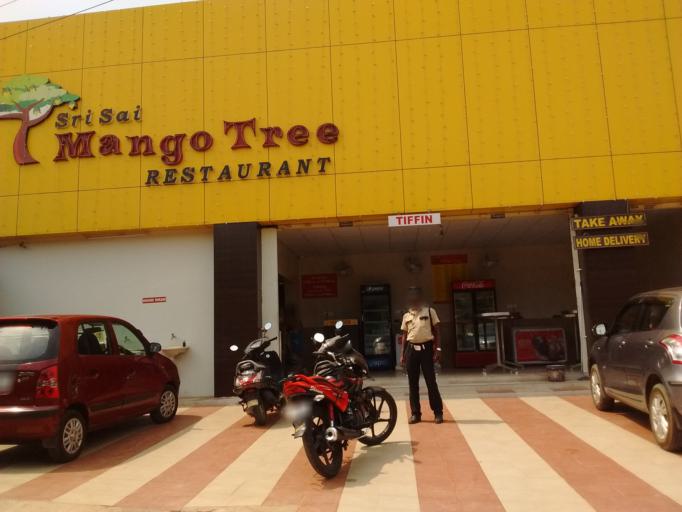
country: IN
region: Andhra Pradesh
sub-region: Krishna
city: Yanamalakuduru
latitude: 16.5214
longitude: 80.6756
